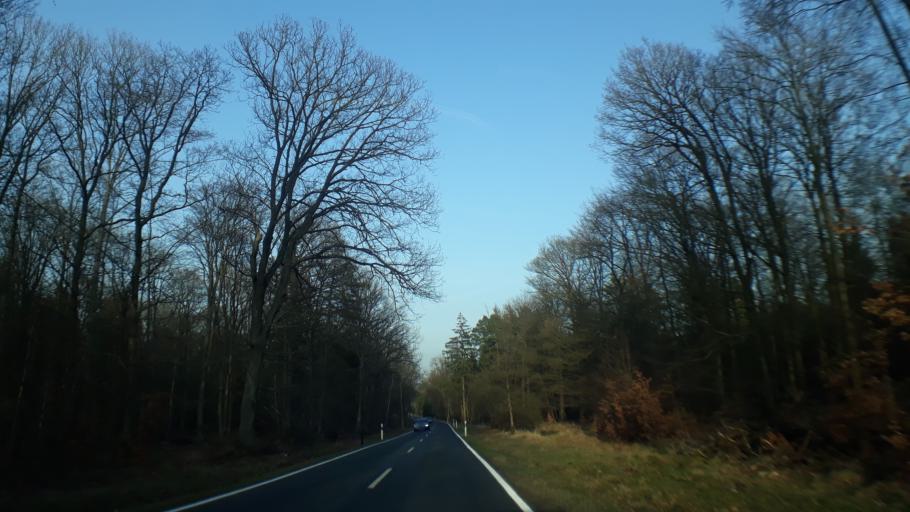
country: DE
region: North Rhine-Westphalia
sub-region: Regierungsbezirk Koln
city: Bad Munstereifel
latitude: 50.5503
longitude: 6.8243
